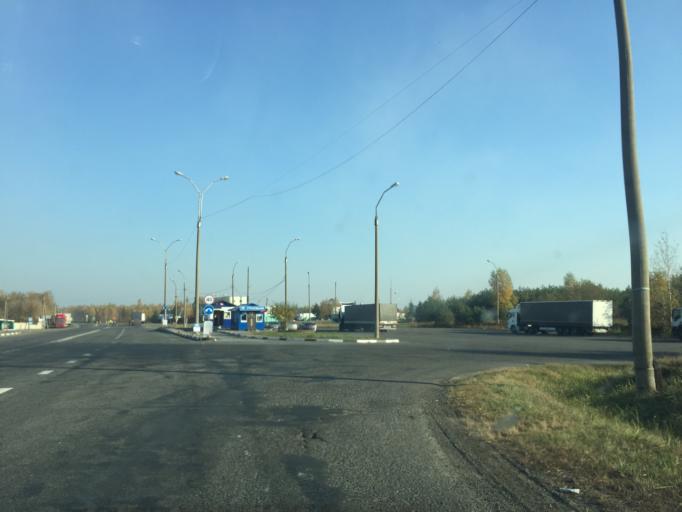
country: BY
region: Gomel
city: Dobrush
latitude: 52.3883
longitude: 31.4632
